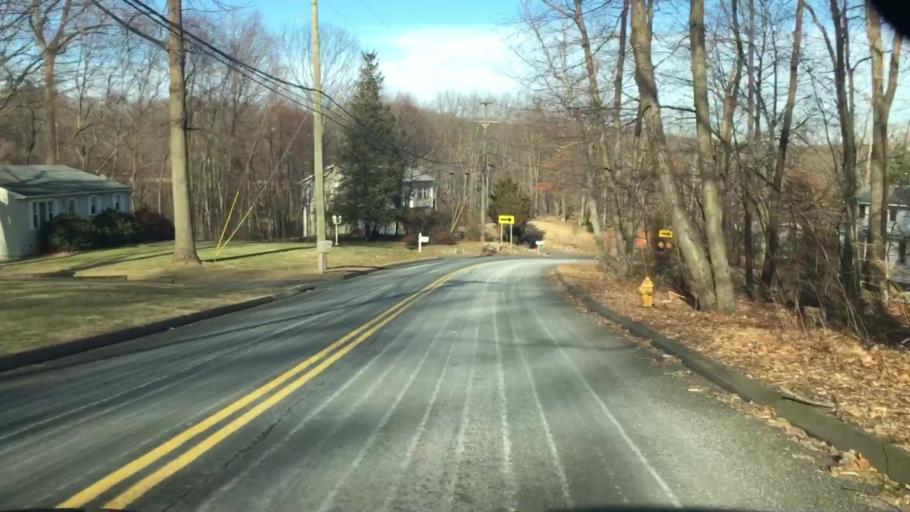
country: US
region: Connecticut
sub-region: New Haven County
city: Prospect
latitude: 41.5391
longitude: -72.9505
